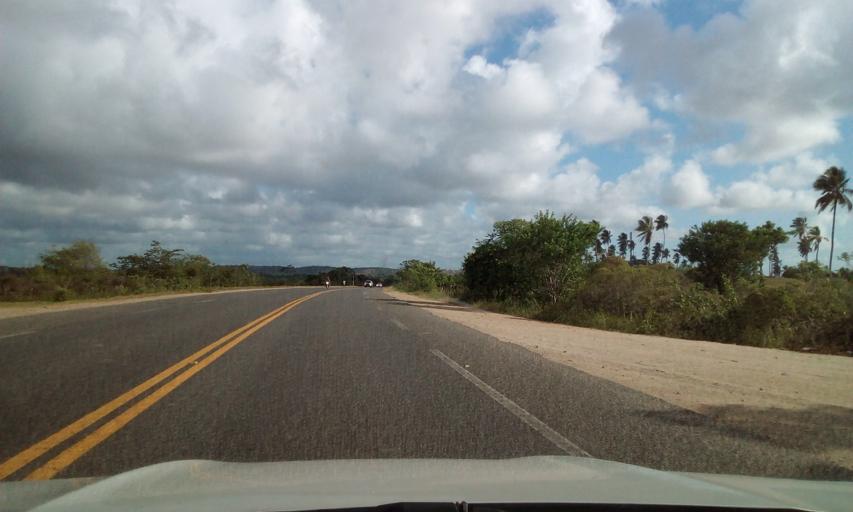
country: BR
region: Bahia
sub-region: Conde
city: Conde
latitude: -11.8153
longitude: -37.6350
